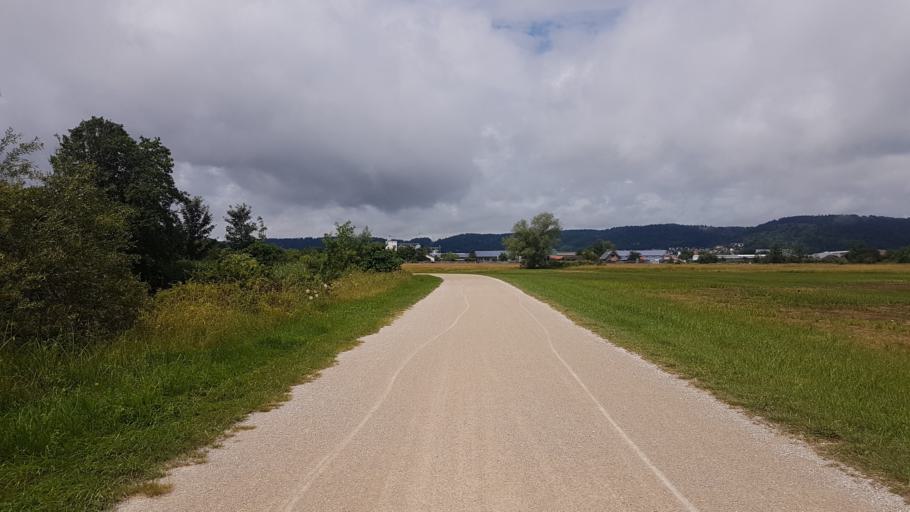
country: DE
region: Bavaria
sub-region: Upper Palatinate
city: Dietfurt
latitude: 49.0188
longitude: 11.5963
